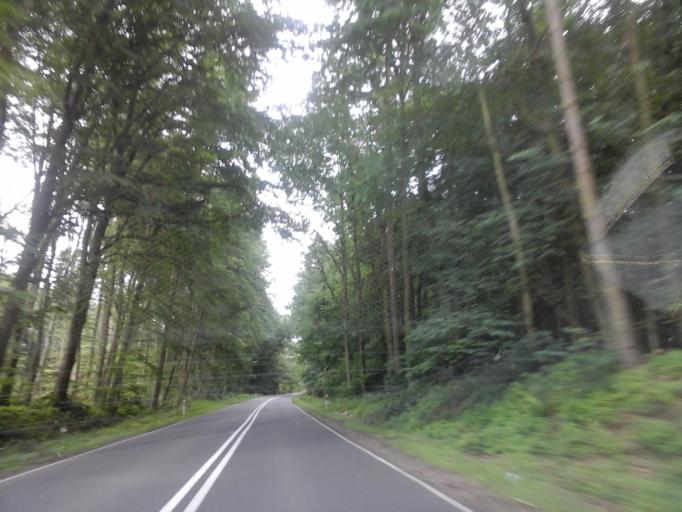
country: PL
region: West Pomeranian Voivodeship
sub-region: Powiat stargardzki
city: Suchan
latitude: 53.2729
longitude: 15.3279
